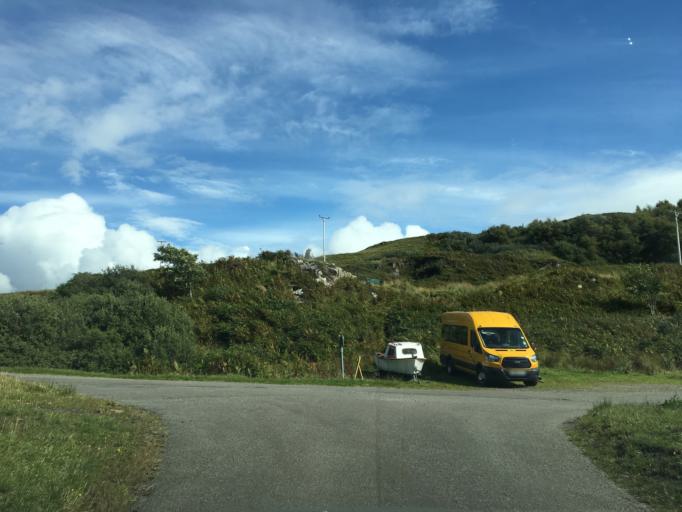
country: GB
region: Scotland
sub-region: Argyll and Bute
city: Oban
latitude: 56.2467
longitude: -5.6393
